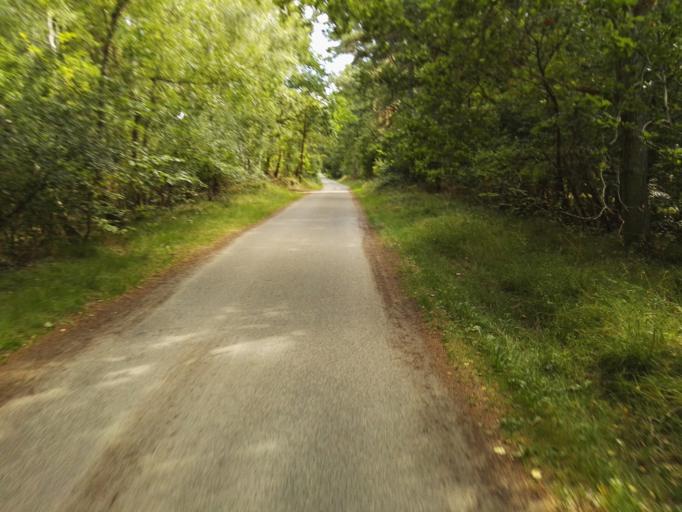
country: DK
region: Zealand
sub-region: Odsherred Kommune
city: Nykobing Sjaelland
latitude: 55.9444
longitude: 11.7013
